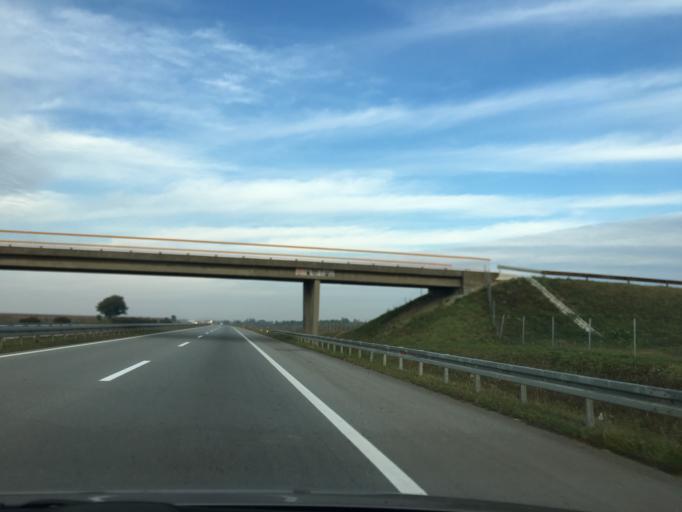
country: RS
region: Autonomna Pokrajina Vojvodina
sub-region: Juznobacki Okrug
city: Kovilj
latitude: 45.2584
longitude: 19.9988
